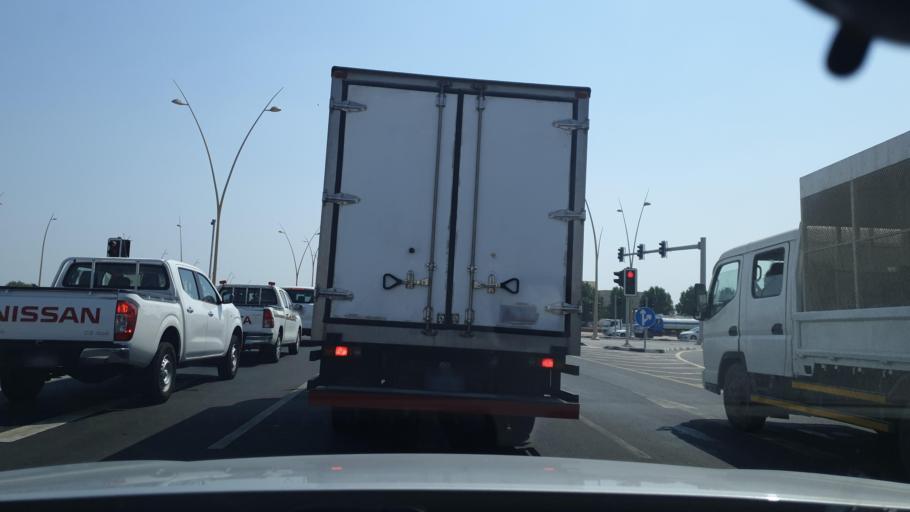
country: QA
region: Al Khawr
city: Al Khawr
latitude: 25.6809
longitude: 51.4964
